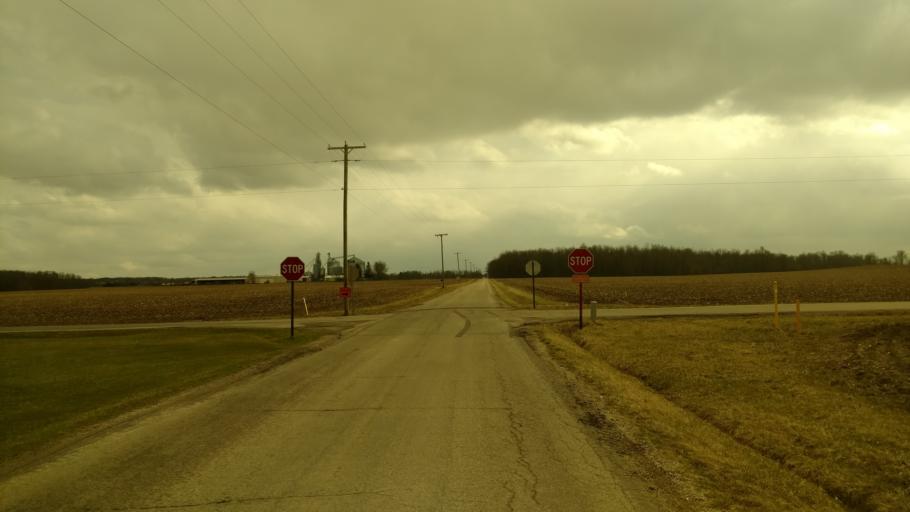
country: US
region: Ohio
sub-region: Crawford County
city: Crestline
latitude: 40.8144
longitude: -82.6968
